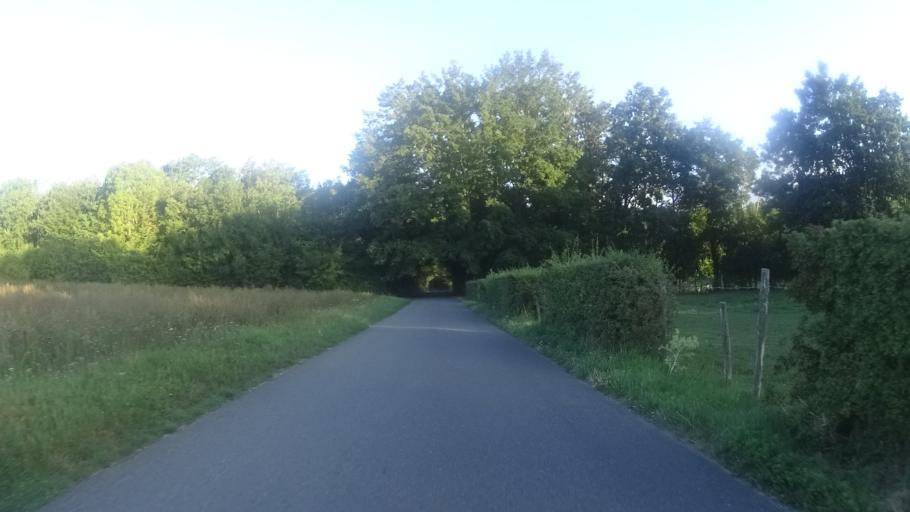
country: FR
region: Picardie
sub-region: Departement de l'Oise
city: Ver-sur-Launette
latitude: 49.1742
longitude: 2.6790
